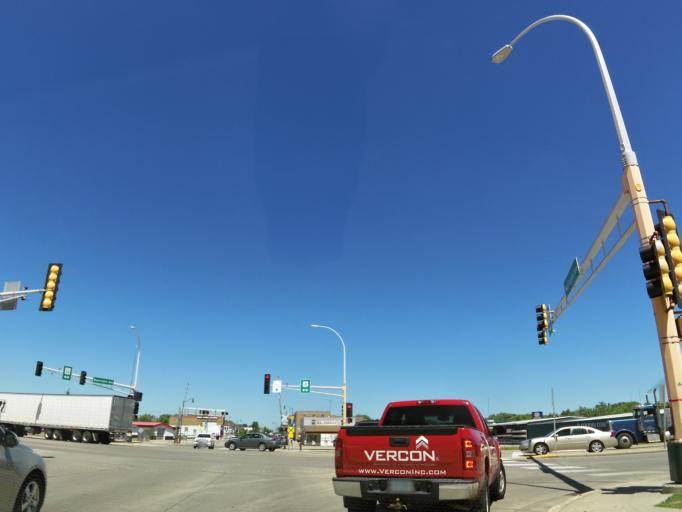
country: US
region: Minnesota
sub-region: Becker County
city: Detroit Lakes
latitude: 46.8189
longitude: -95.8452
